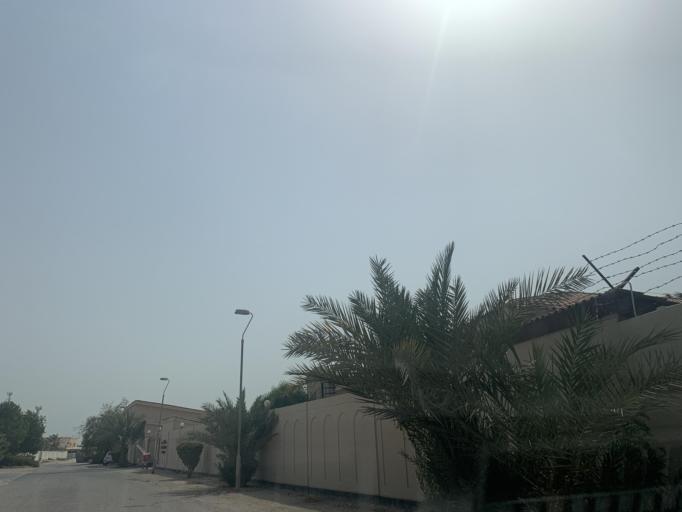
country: BH
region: Manama
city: Jidd Hafs
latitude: 26.1994
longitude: 50.4751
